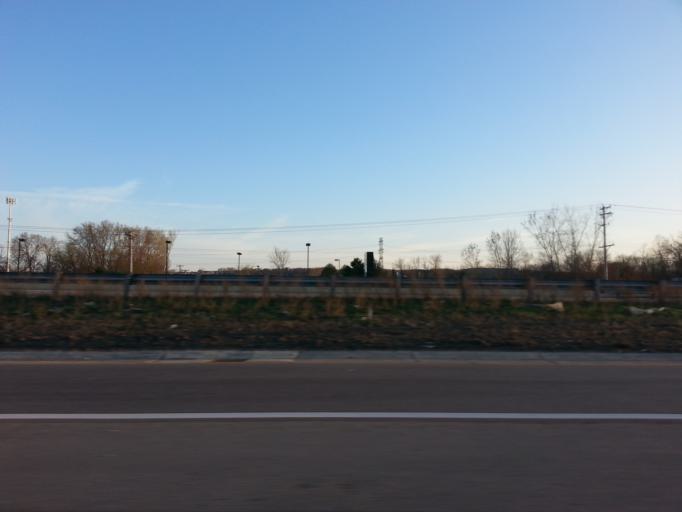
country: US
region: Minnesota
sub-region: Scott County
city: Savage
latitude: 44.7797
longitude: -93.3815
